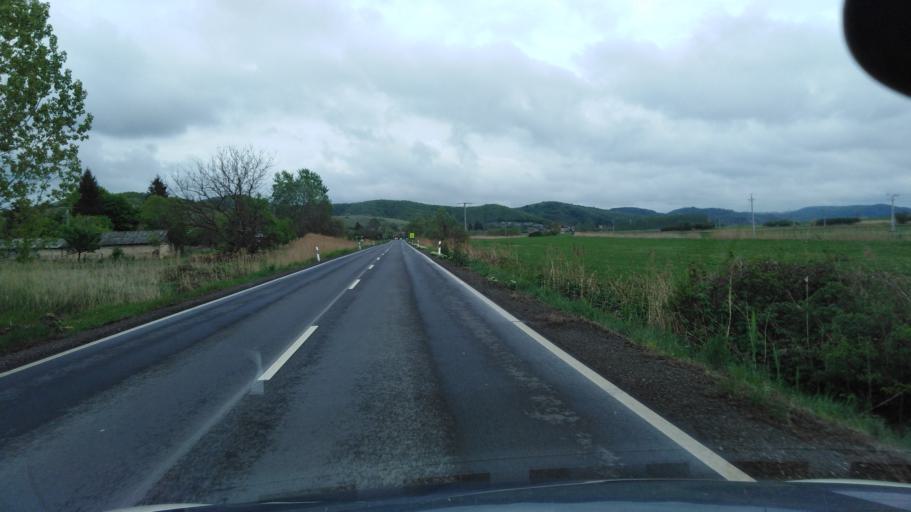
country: HU
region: Nograd
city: Karancskeszi
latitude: 48.1135
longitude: 19.6602
